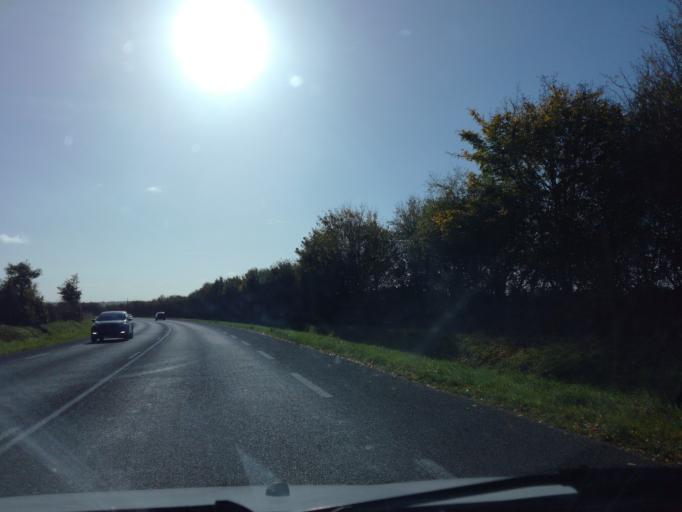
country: FR
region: Pays de la Loire
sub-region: Departement de Maine-et-Loire
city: Pouance
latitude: 47.7705
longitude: -1.2274
